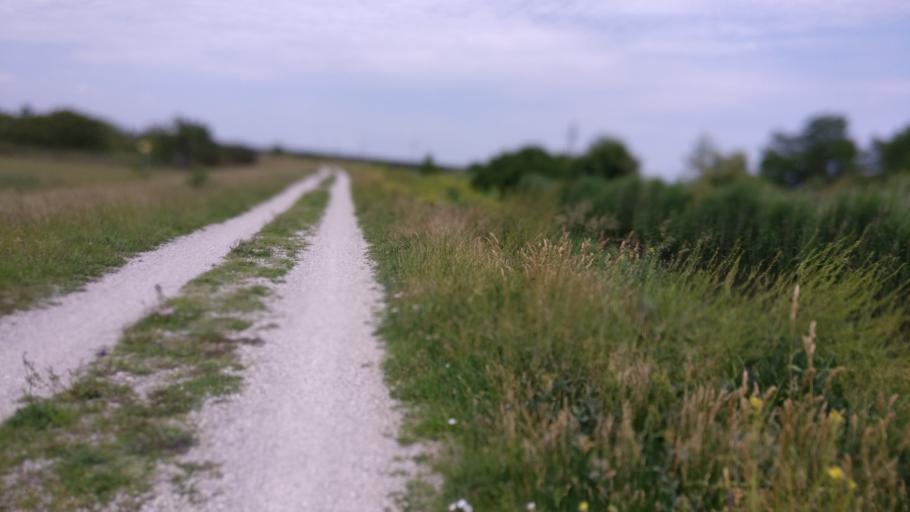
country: AT
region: Lower Austria
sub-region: Politischer Bezirk Wiener Neustadt
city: Lichtenworth
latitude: 47.8506
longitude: 16.2782
